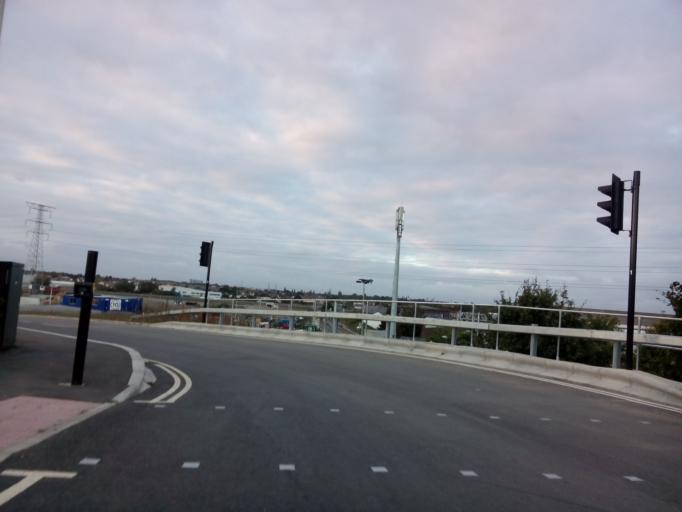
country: GB
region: England
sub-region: Suffolk
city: Ipswich
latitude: 52.0585
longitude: 1.1265
